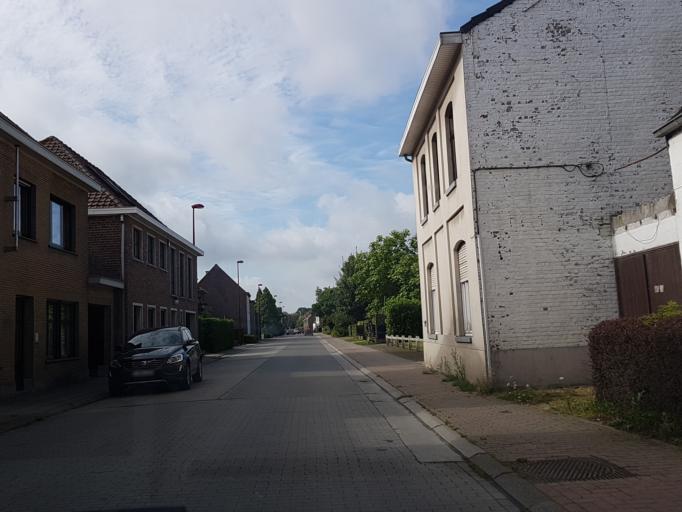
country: BE
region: Flanders
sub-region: Provincie Oost-Vlaanderen
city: Nevele
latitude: 51.0642
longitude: 3.5759
